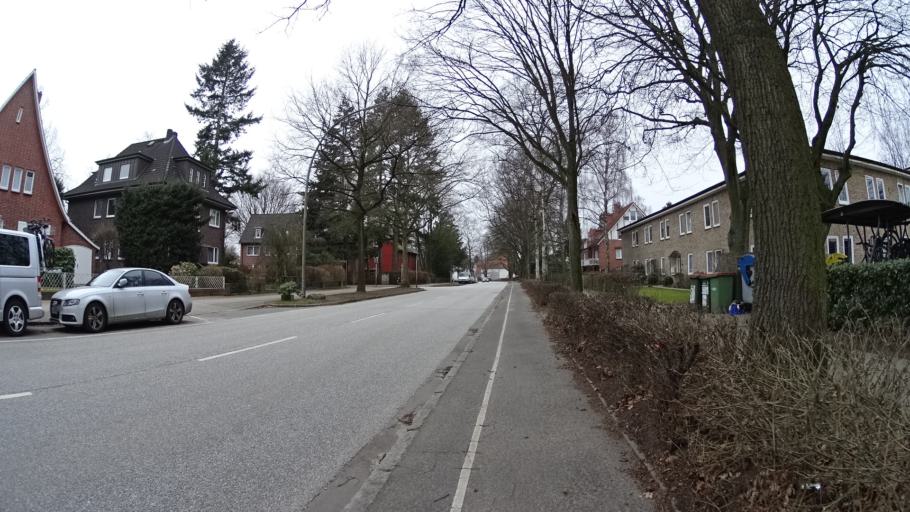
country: DE
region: Hamburg
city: Eidelstedt
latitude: 53.5653
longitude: 9.8840
